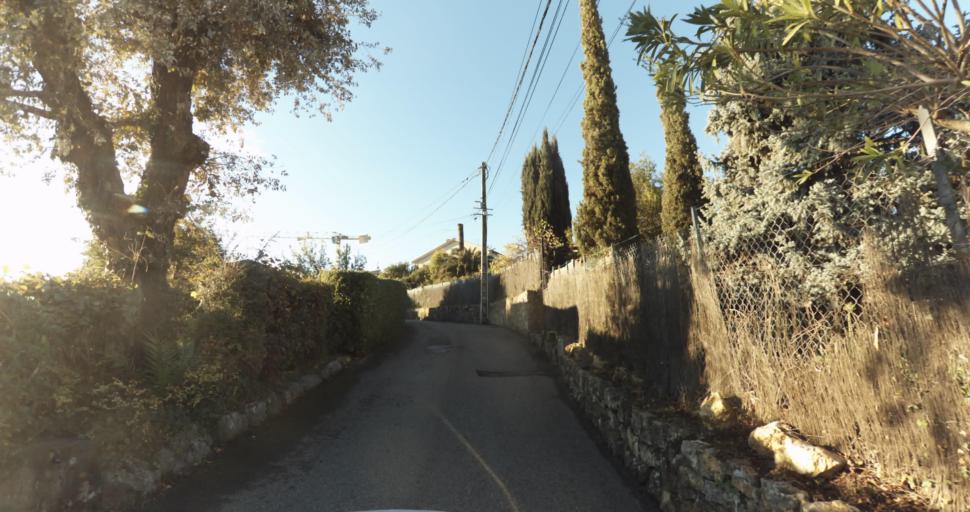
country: FR
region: Provence-Alpes-Cote d'Azur
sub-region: Departement des Alpes-Maritimes
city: Vence
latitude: 43.7230
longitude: 7.1222
